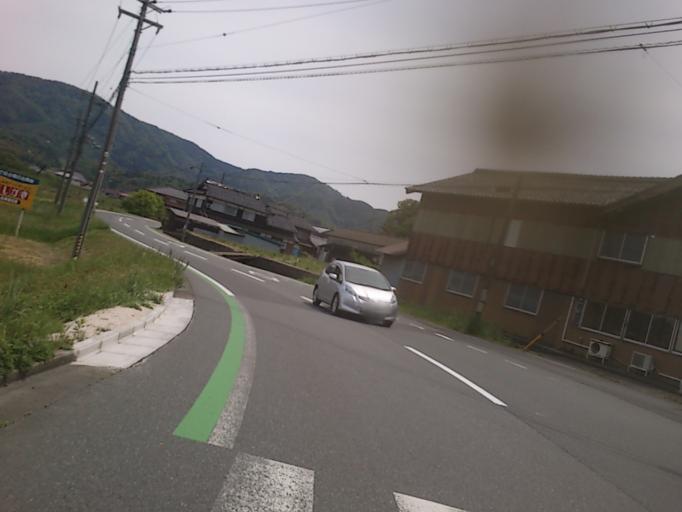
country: JP
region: Kyoto
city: Miyazu
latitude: 35.6582
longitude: 135.0876
